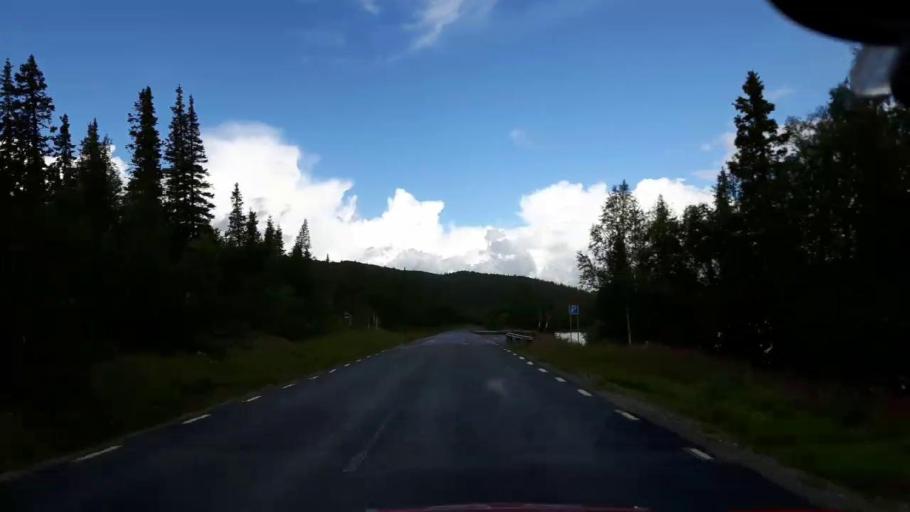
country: SE
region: Vaesterbotten
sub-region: Vilhelmina Kommun
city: Sjoberg
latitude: 65.0094
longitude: 15.1799
